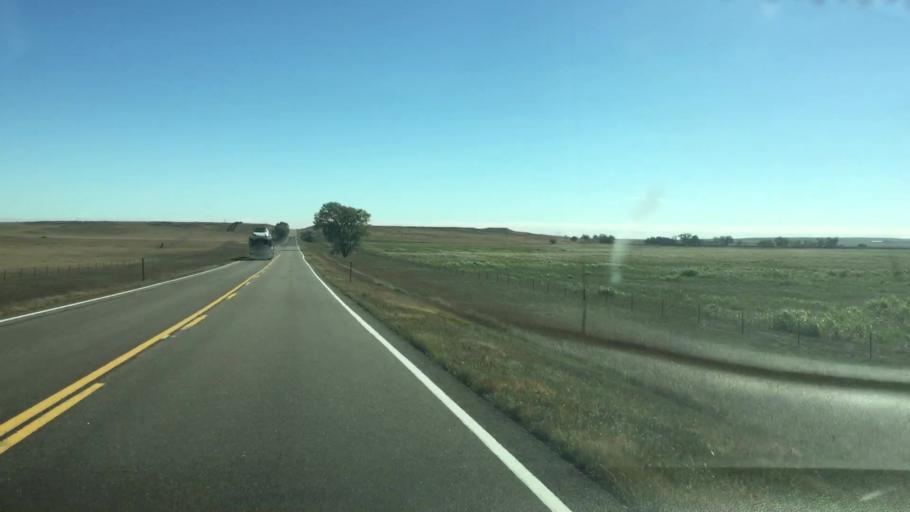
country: US
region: Colorado
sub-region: Lincoln County
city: Limon
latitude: 39.2947
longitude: -103.8942
